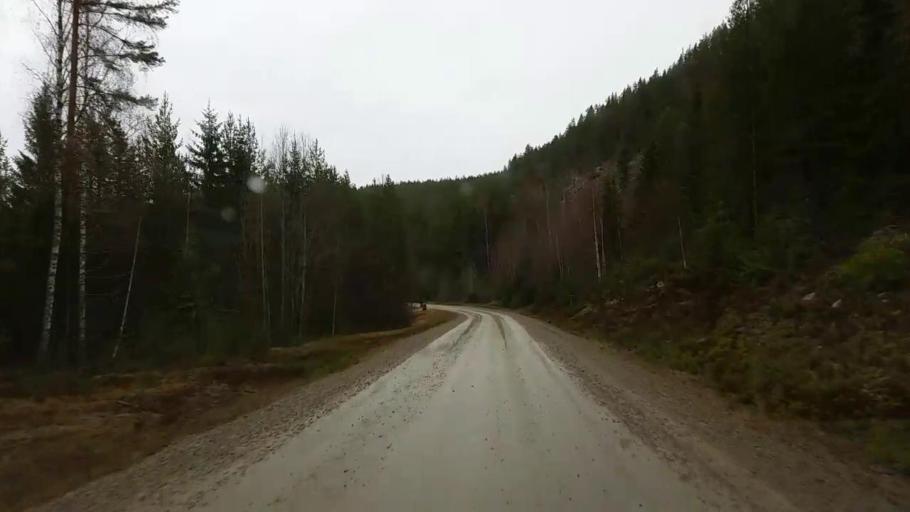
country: SE
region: Gaevleborg
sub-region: Ljusdals Kommun
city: Farila
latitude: 62.0263
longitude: 15.8229
